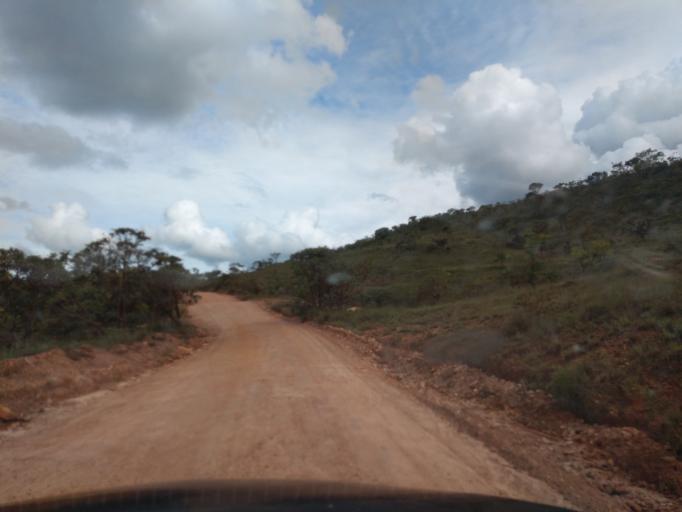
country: BR
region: Minas Gerais
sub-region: Lavras
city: Lavras
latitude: -21.5271
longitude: -44.8911
